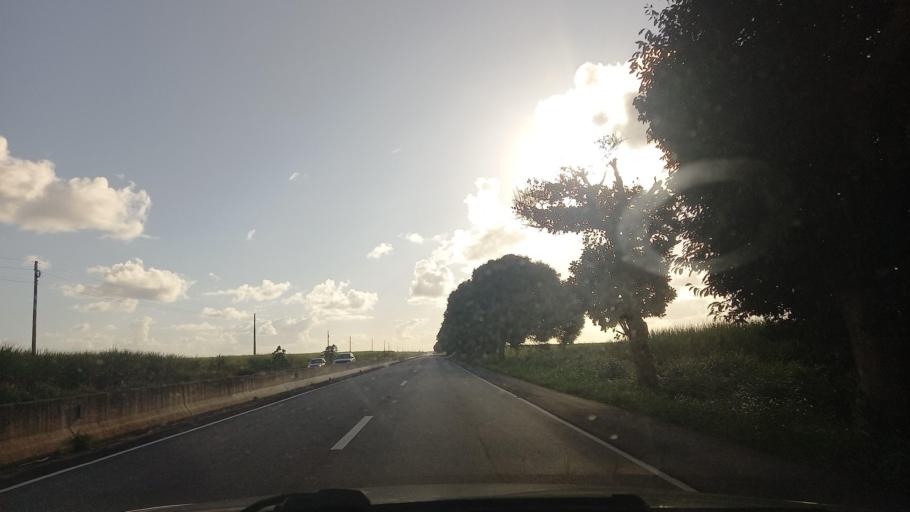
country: BR
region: Alagoas
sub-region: Sao Miguel Dos Campos
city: Sao Miguel dos Campos
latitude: -9.8031
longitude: -36.1417
